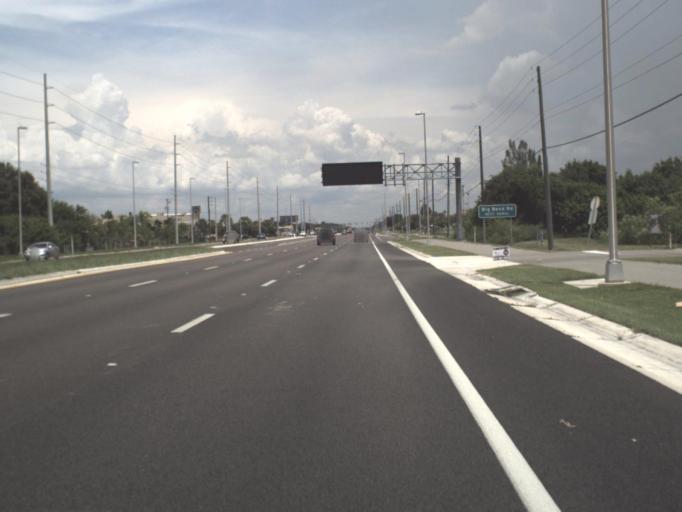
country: US
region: Florida
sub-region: Hillsborough County
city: Sun City Center
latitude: 27.7862
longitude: -82.3348
